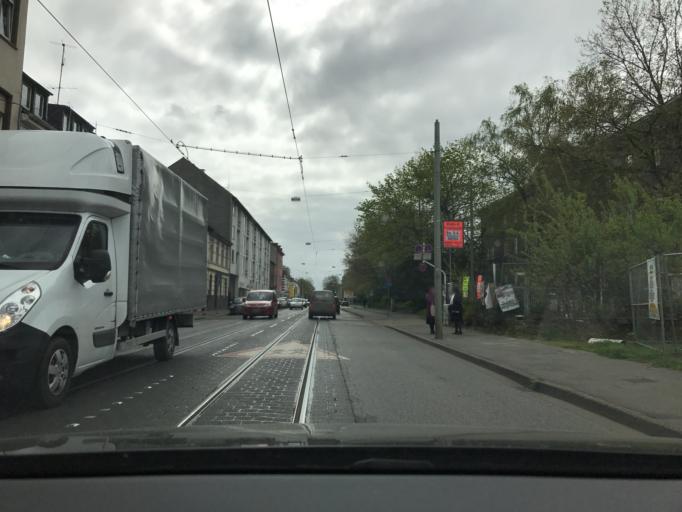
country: DE
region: North Rhine-Westphalia
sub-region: Regierungsbezirk Dusseldorf
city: Krefeld
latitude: 51.3223
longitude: 6.5704
